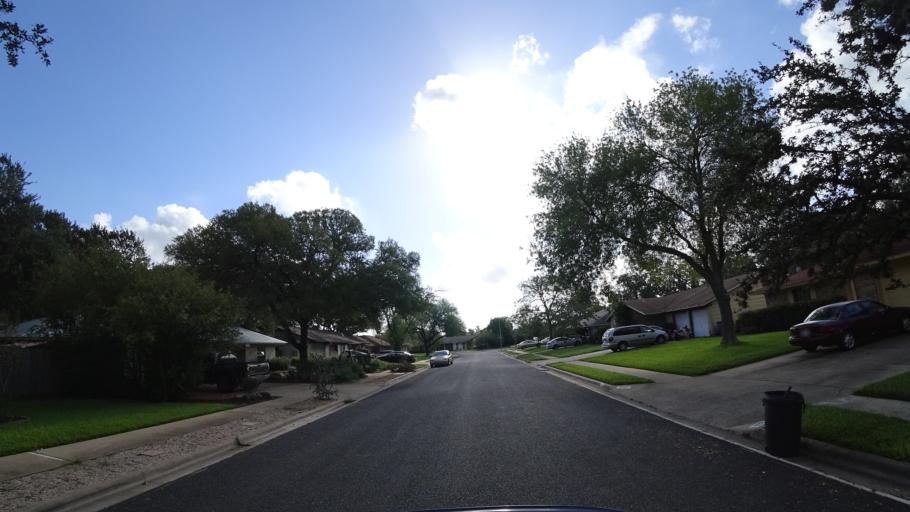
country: US
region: Texas
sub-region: Travis County
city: Rollingwood
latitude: 30.2162
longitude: -97.8017
